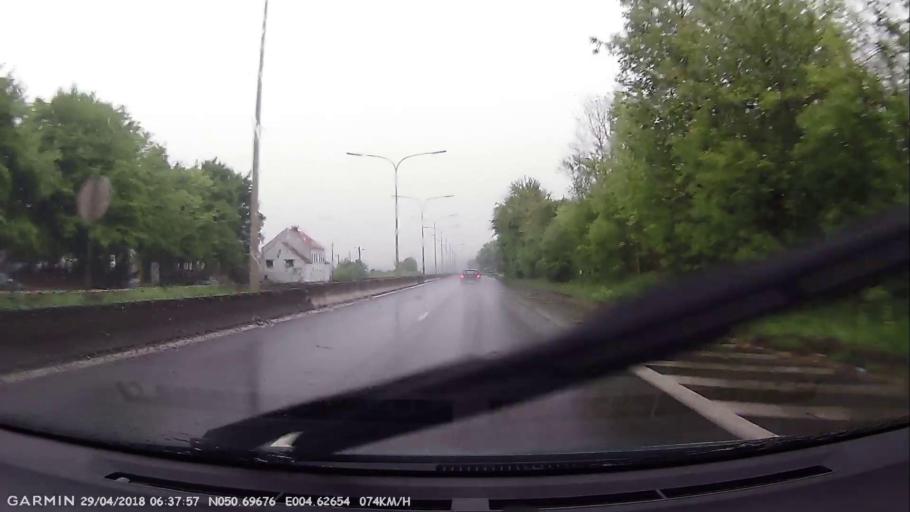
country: BE
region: Wallonia
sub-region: Province du Brabant Wallon
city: Louvain-la-Neuve
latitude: 50.6969
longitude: 4.6267
